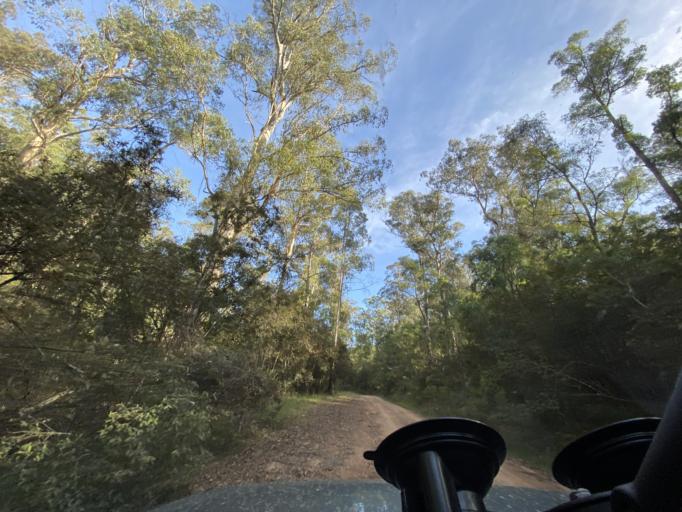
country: AU
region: Victoria
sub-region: Mansfield
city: Mansfield
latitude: -37.5143
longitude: 146.0950
